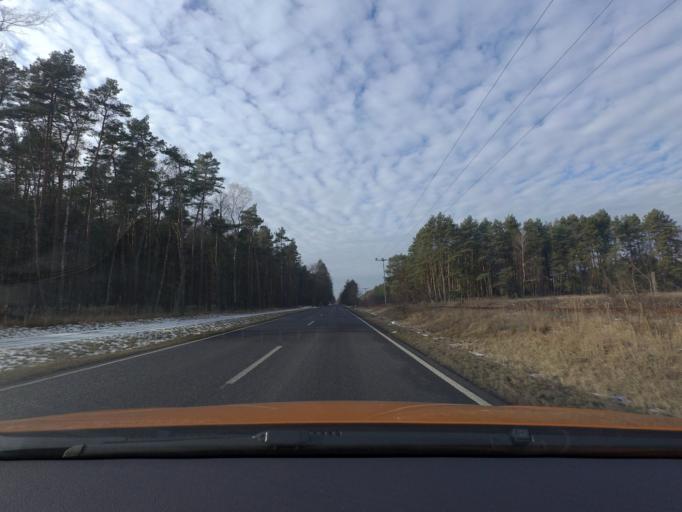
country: DE
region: Brandenburg
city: Schonermark
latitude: 52.8970
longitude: 13.1083
